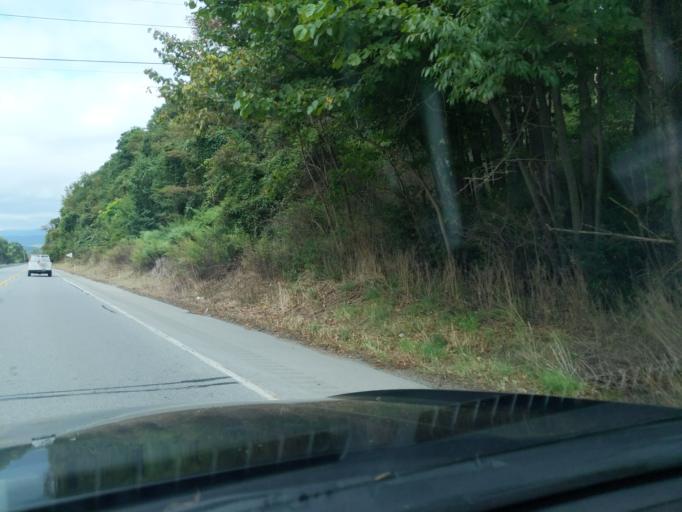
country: US
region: Pennsylvania
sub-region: Blair County
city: Hollidaysburg
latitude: 40.4069
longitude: -78.4025
